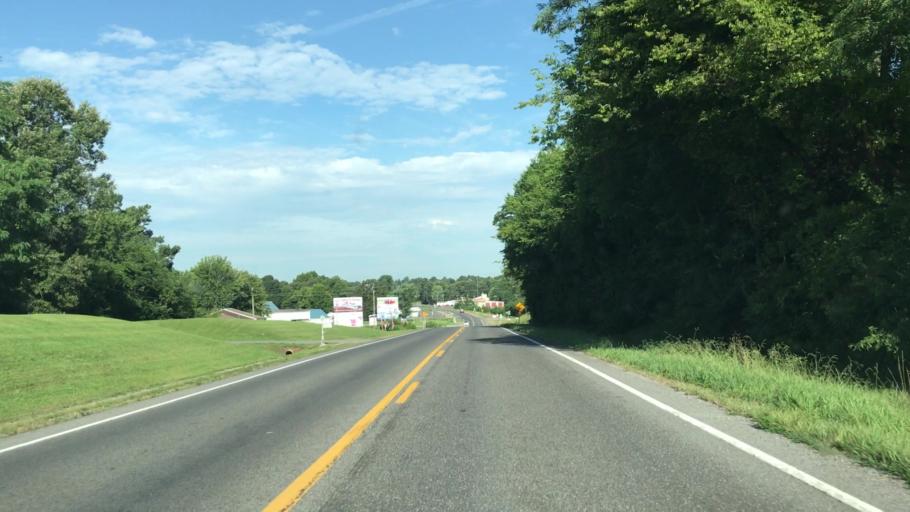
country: US
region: Kentucky
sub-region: Livingston County
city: Ledbetter
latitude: 37.0059
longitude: -88.4253
